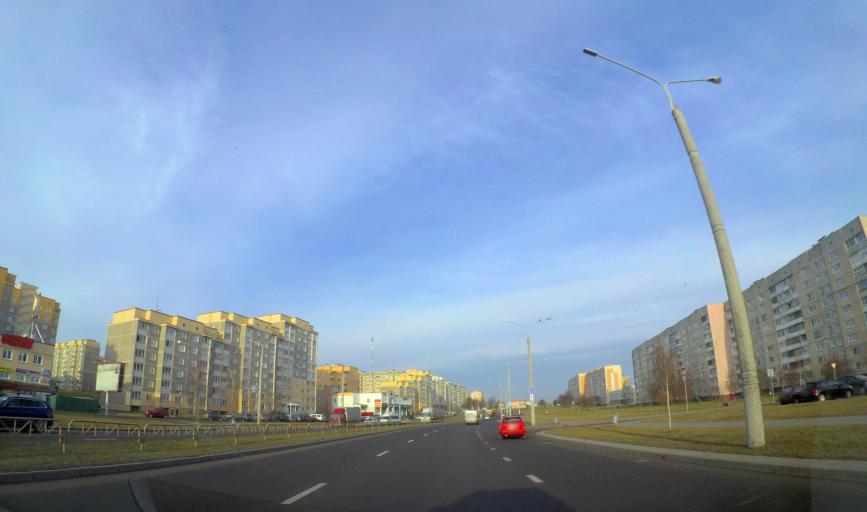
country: BY
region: Grodnenskaya
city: Hrodna
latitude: 53.6589
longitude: 23.7819
